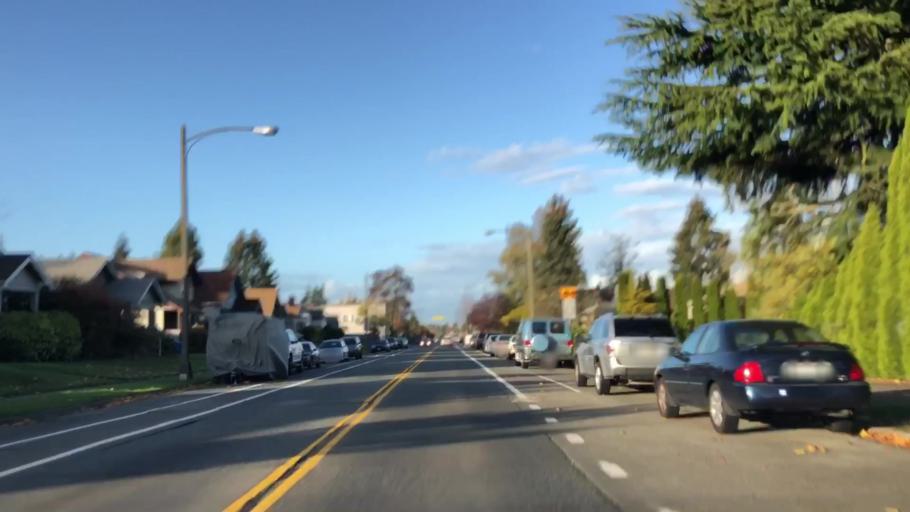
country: US
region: Washington
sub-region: Pierce County
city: Tacoma
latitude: 47.2084
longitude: -122.4432
